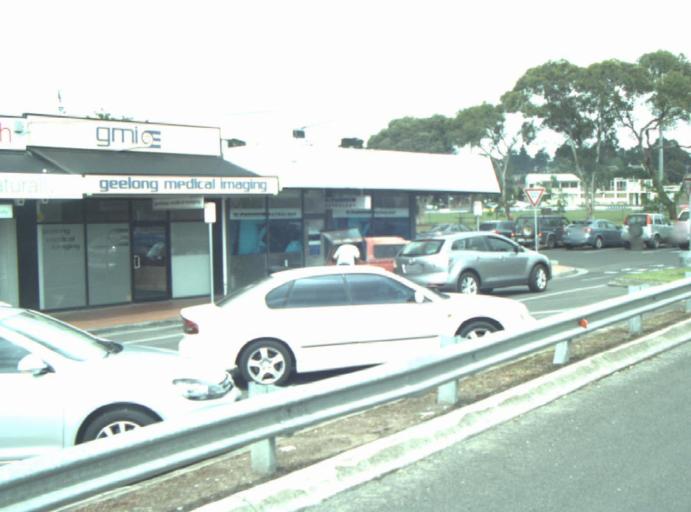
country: AU
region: Victoria
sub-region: Greater Geelong
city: Wandana Heights
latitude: -38.1717
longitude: 144.3235
